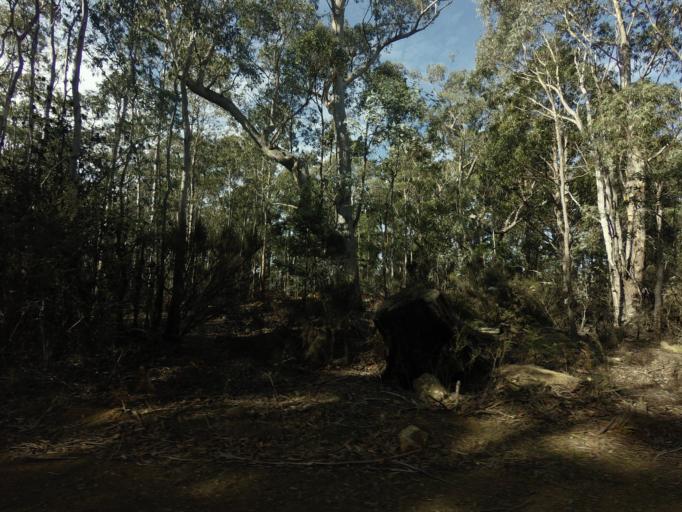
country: AU
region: Tasmania
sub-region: Sorell
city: Sorell
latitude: -42.4943
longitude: 147.4805
